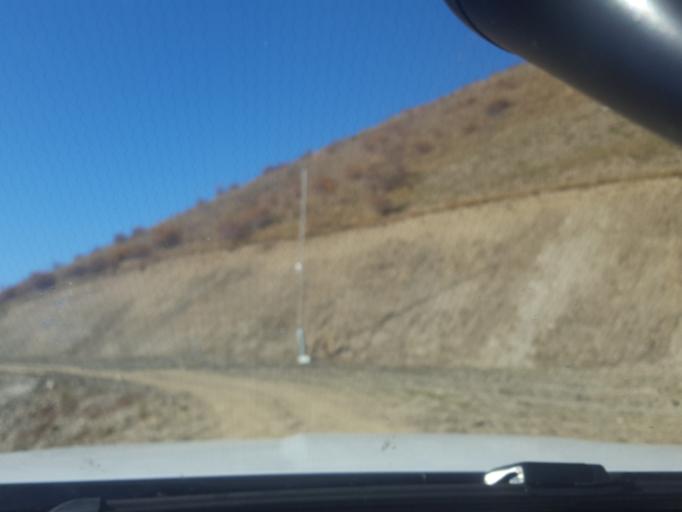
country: FR
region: Rhone-Alpes
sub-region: Departement de la Savoie
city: Saint-Jean-de-Maurienne
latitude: 45.2163
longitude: 6.2644
